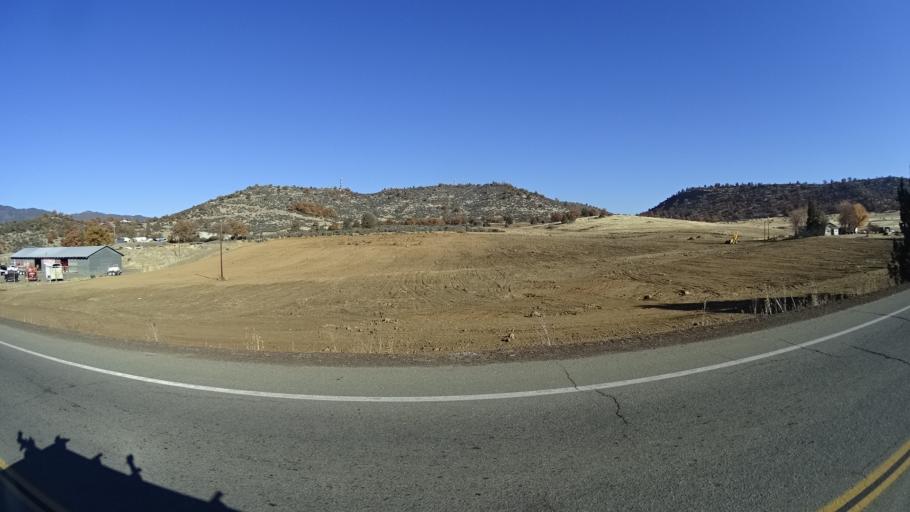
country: US
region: California
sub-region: Siskiyou County
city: Yreka
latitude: 41.7150
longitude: -122.6292
